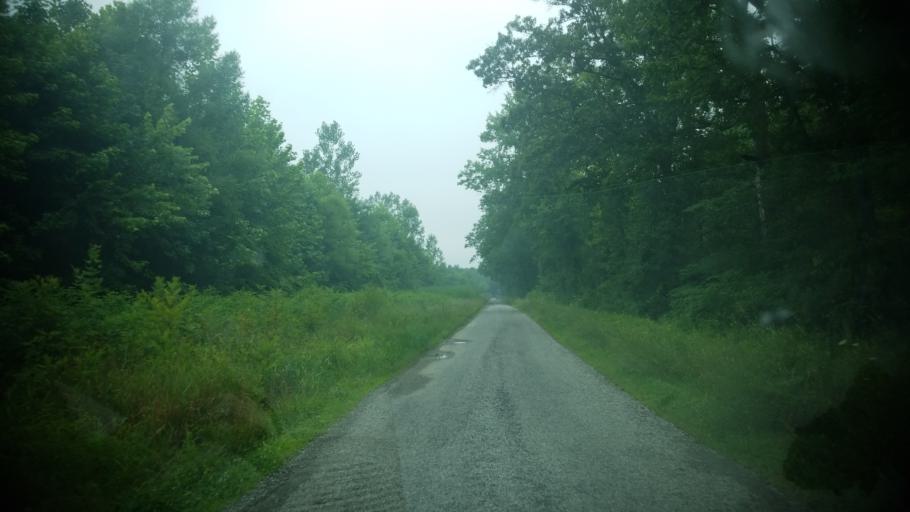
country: US
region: Illinois
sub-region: Clay County
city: Flora
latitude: 38.5734
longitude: -88.3688
